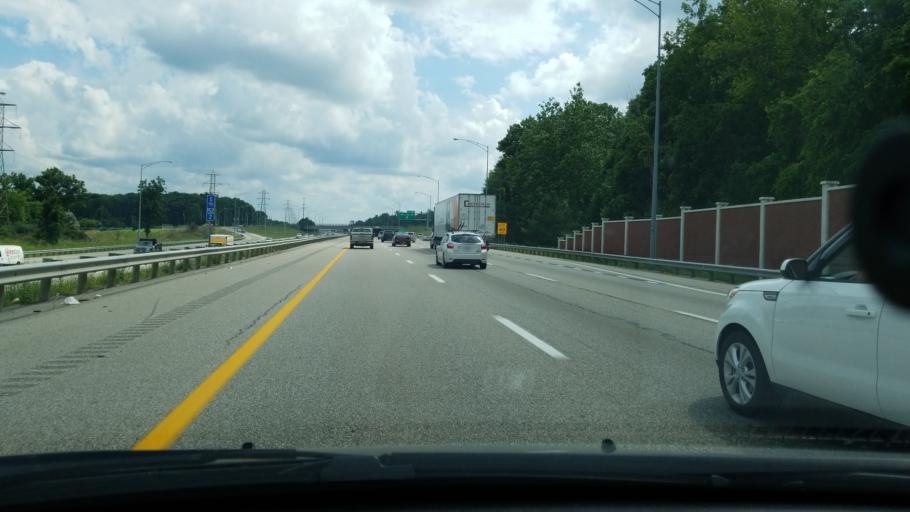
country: US
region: Ohio
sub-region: Cuyahoga County
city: Independence
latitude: 41.3501
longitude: -81.6498
